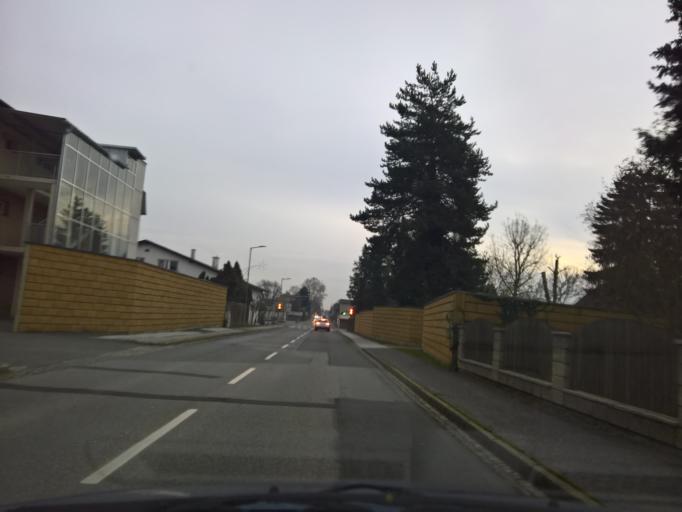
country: AT
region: Styria
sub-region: Politischer Bezirk Leibnitz
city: Leibnitz
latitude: 46.7725
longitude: 15.5560
